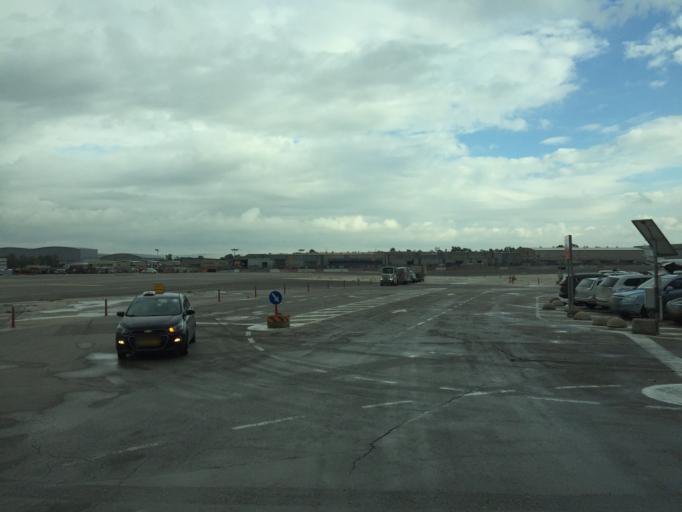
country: IL
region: Central District
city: Yehud
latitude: 31.9958
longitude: 34.8973
